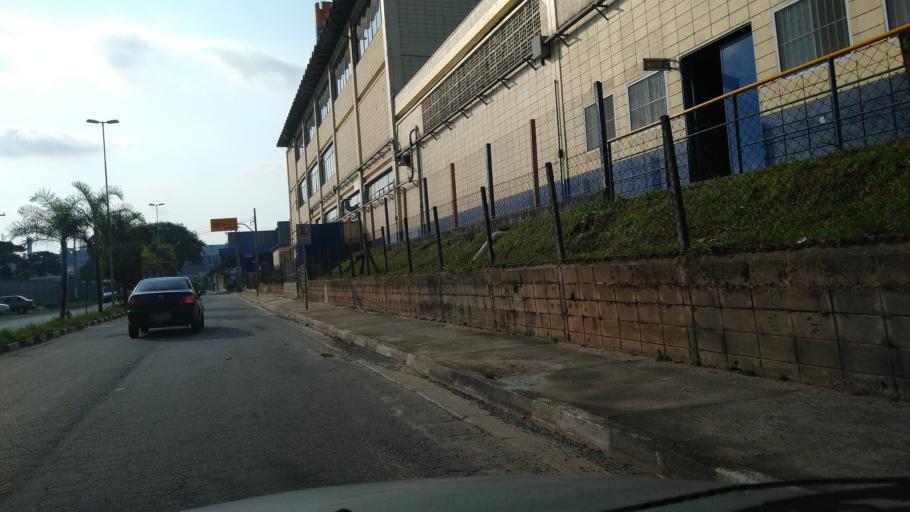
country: BR
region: Sao Paulo
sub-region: Guarulhos
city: Guarulhos
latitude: -23.4907
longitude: -46.5409
